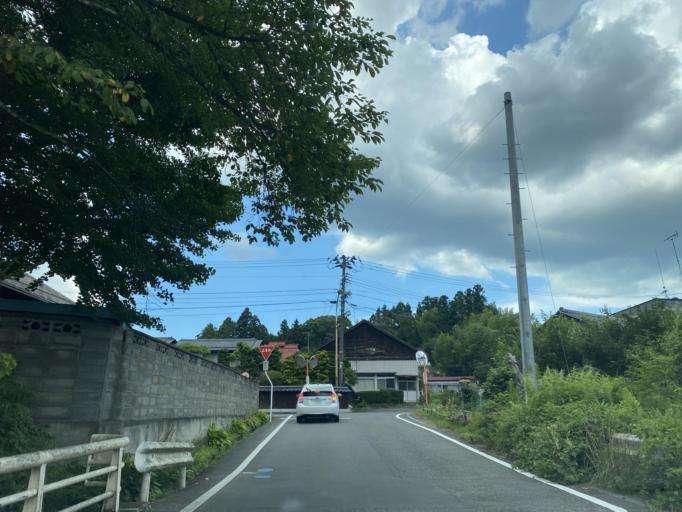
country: JP
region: Fukushima
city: Koriyama
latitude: 37.3707
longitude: 140.4299
